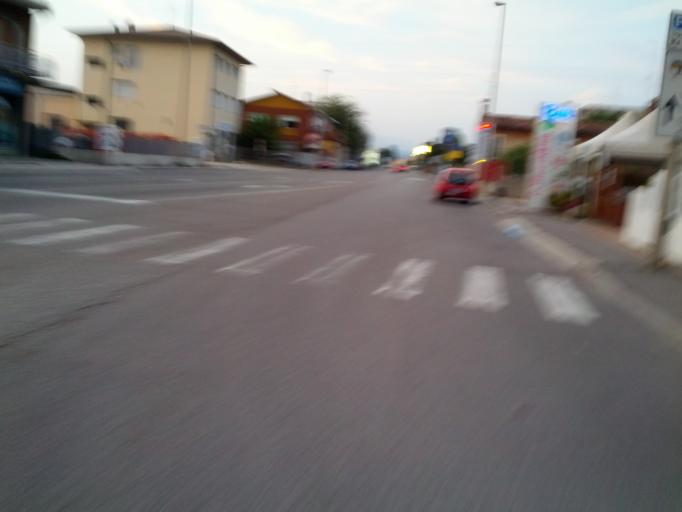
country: IT
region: Veneto
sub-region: Provincia di Verona
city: Verona
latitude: 45.4078
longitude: 10.9630
